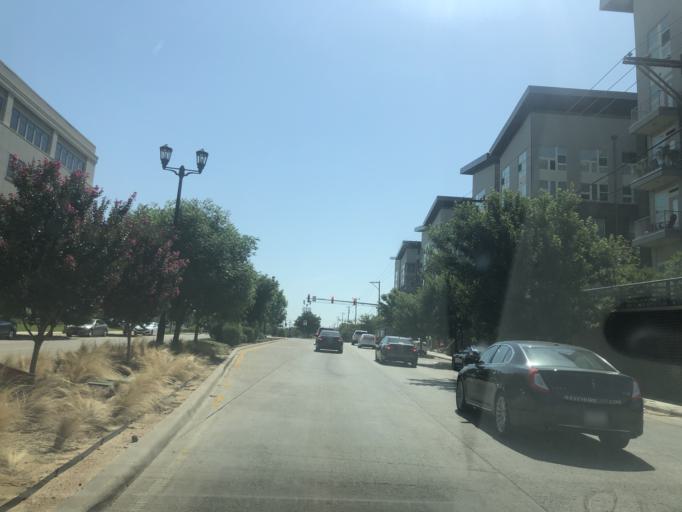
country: US
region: Texas
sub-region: Tarrant County
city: Fort Worth
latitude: 32.7332
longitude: -97.3430
